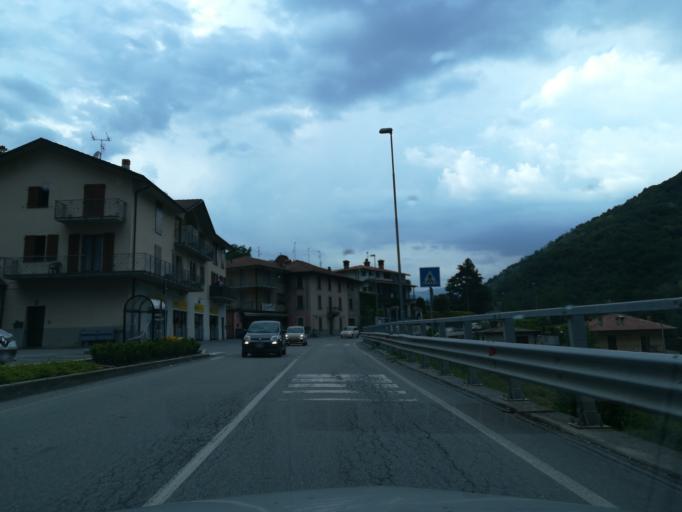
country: IT
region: Lombardy
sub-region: Provincia di Bergamo
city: Almenno San Salvatore
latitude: 45.7622
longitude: 9.5910
